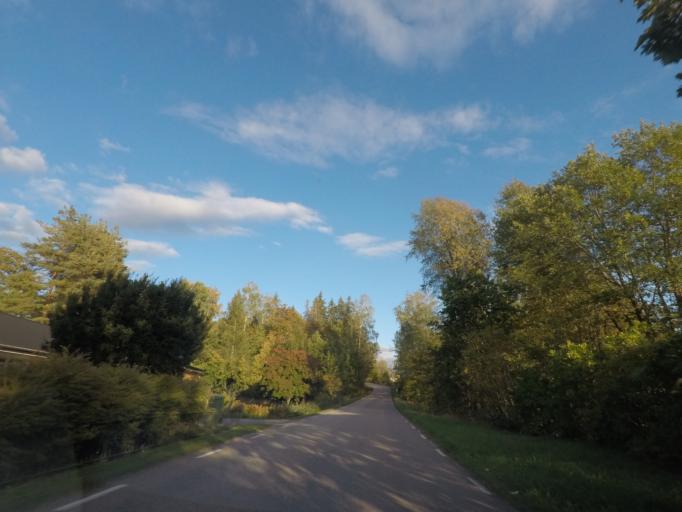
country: SE
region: Vaestmanland
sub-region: Kopings Kommun
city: Koping
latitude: 59.5100
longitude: 16.0739
